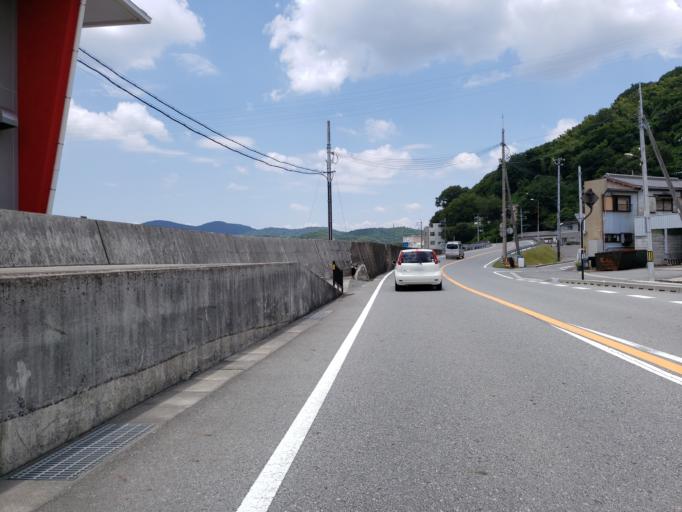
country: JP
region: Hyogo
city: Aioi
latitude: 34.7987
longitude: 134.4700
